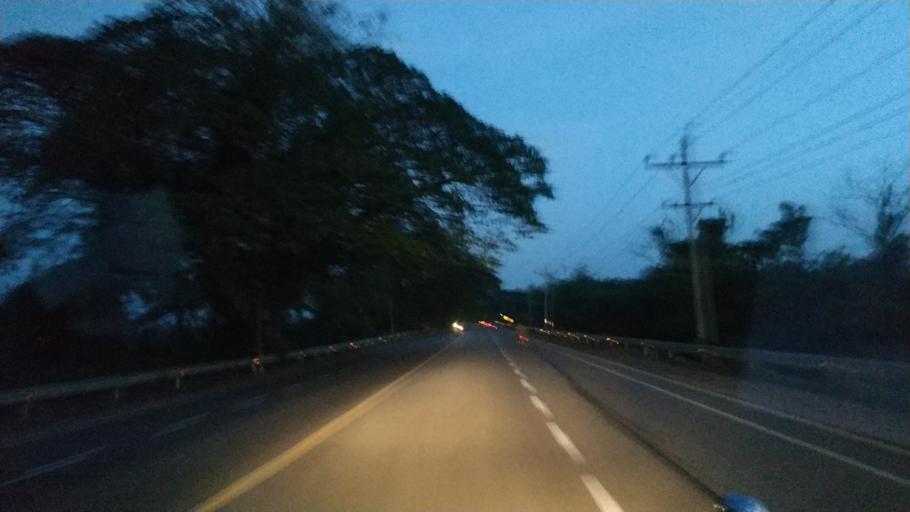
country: MM
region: Mon
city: Kyaikto
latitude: 17.3502
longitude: 97.0385
